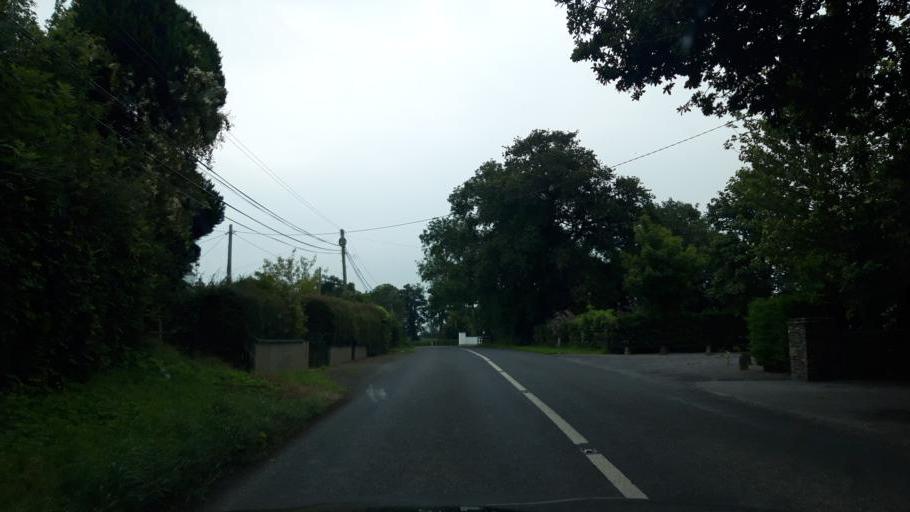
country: IE
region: Munster
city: Fethard
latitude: 52.5436
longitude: -7.6811
